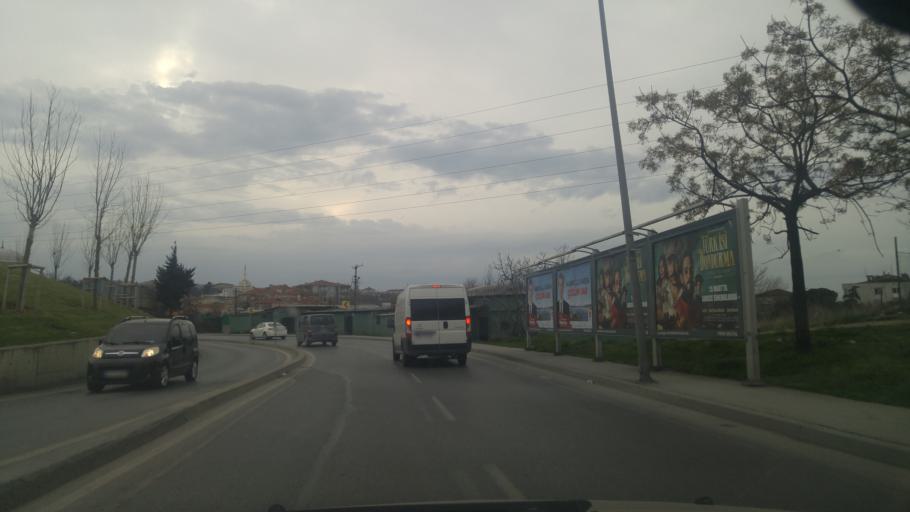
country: TR
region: Istanbul
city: Mahmutbey
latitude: 40.9850
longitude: 28.7673
